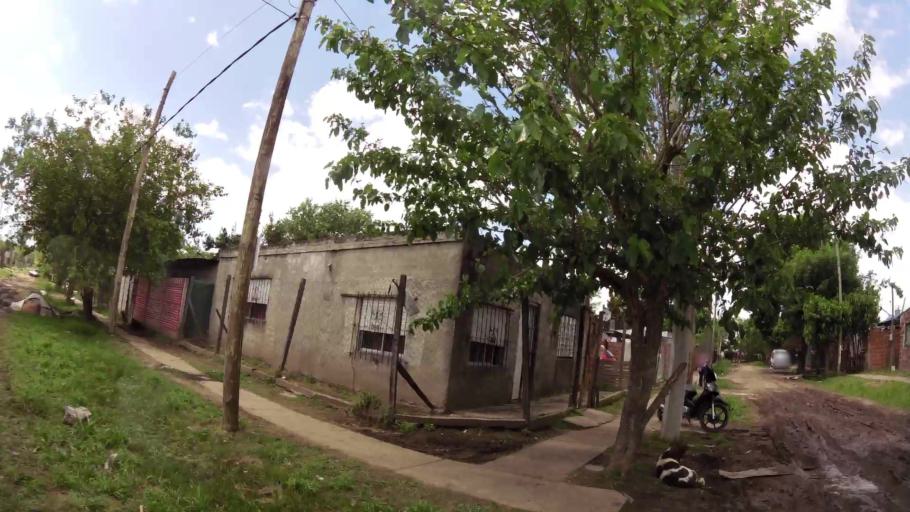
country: AR
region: Buenos Aires
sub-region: Partido de Quilmes
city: Quilmes
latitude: -34.8200
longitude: -58.2475
